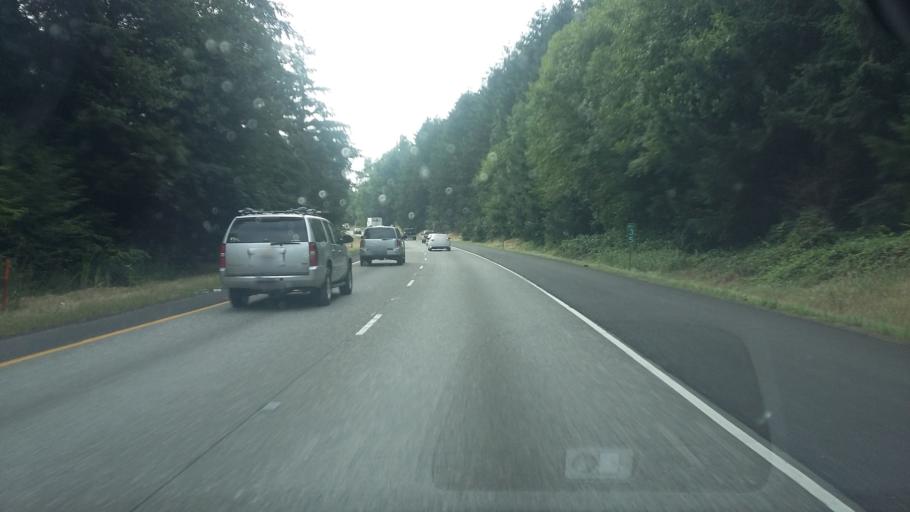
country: US
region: Washington
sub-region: Clark County
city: Salmon Creek
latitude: 45.7003
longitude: -122.6246
